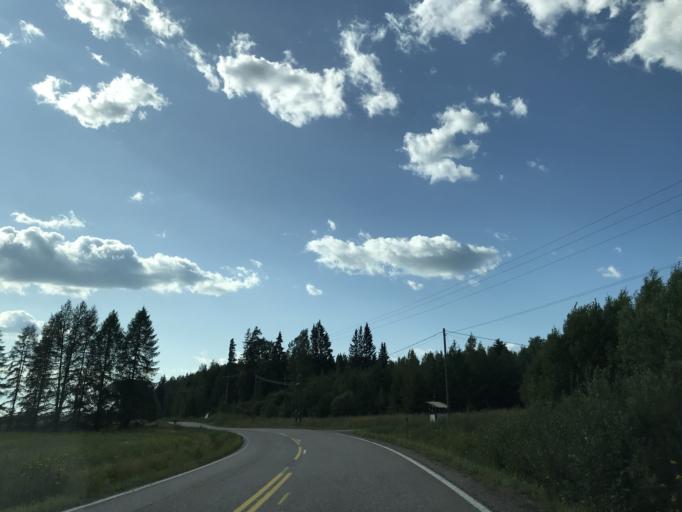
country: FI
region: Uusimaa
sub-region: Helsinki
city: Nurmijaervi
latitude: 60.4511
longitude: 24.6400
